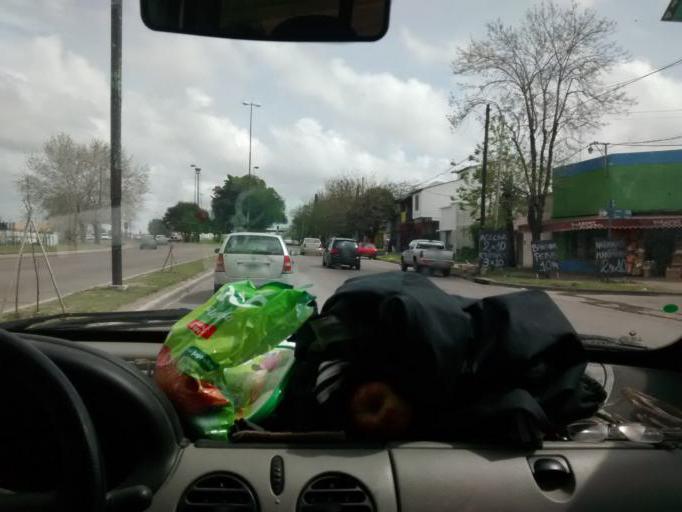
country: AR
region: Buenos Aires
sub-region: Partido de La Plata
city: La Plata
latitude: -34.9405
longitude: -57.9703
